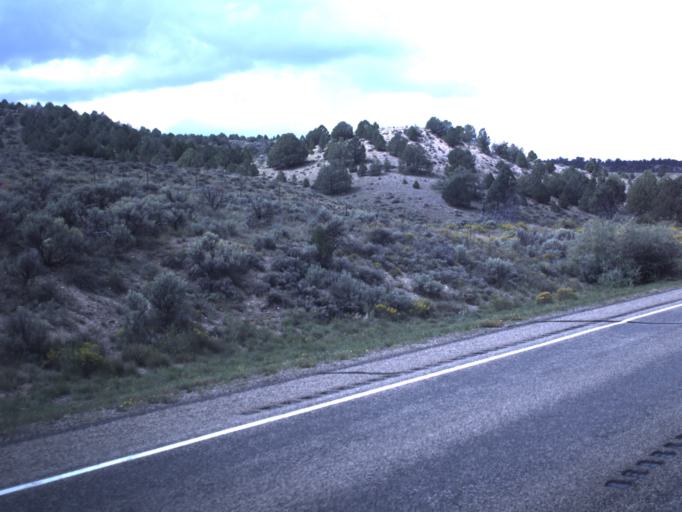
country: US
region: Utah
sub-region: Garfield County
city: Panguitch
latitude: 37.6865
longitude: -112.4006
